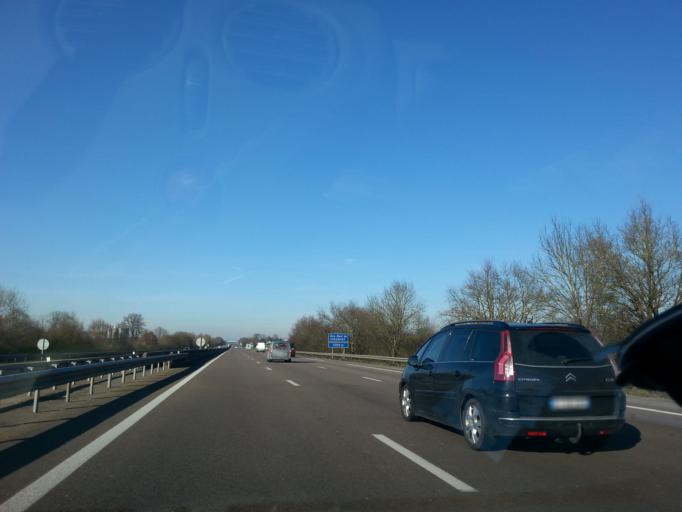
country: FR
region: Haute-Normandie
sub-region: Departement de l'Eure
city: Saint-Pierre-du-Vauvray
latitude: 49.1956
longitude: 1.2298
